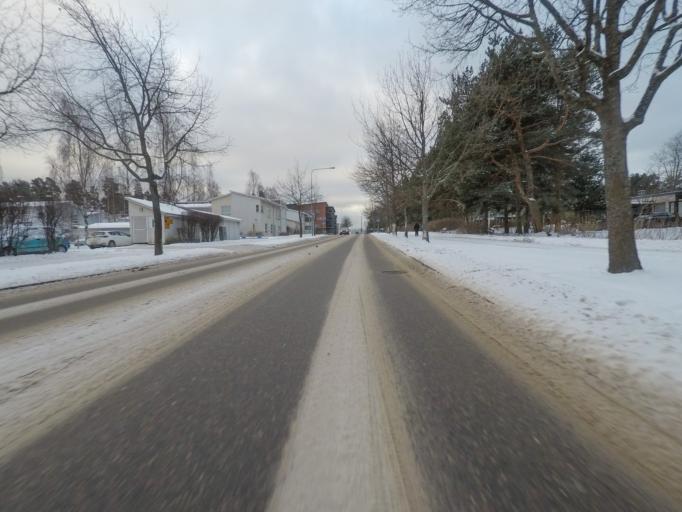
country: FI
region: Uusimaa
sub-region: Helsinki
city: Vantaa
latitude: 60.2118
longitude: 25.1499
